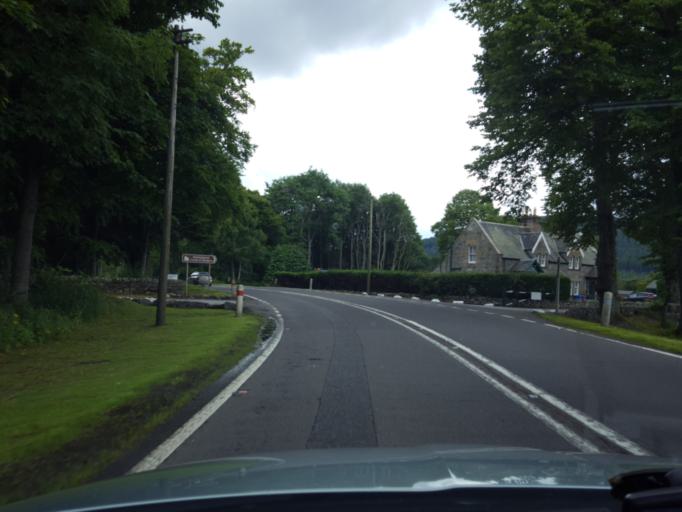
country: GB
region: Scotland
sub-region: Moray
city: Rothes
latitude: 57.4121
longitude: -3.3582
